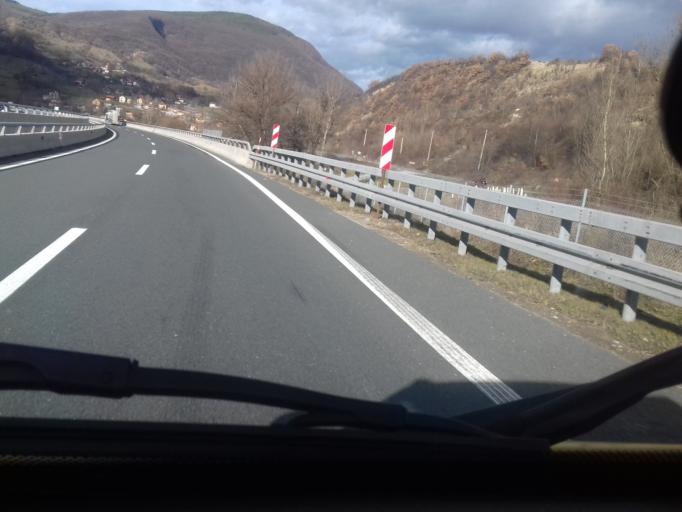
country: BA
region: Federation of Bosnia and Herzegovina
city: Kakanj
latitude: 44.1335
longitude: 18.0839
